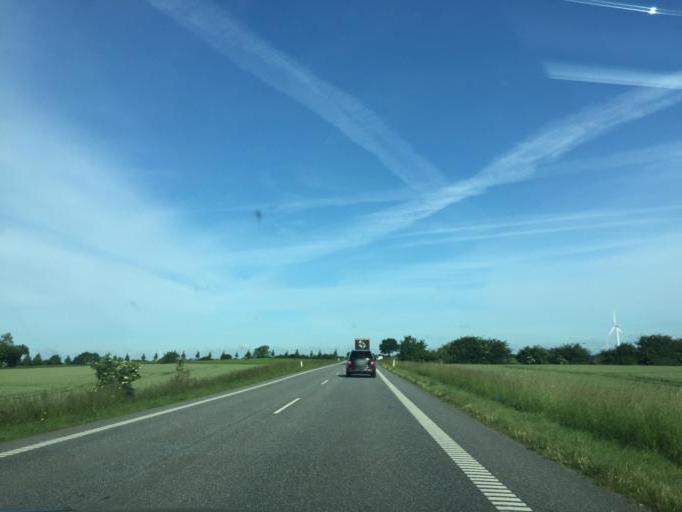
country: DK
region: South Denmark
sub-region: Middelfart Kommune
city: Ejby
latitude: 55.4577
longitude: 9.9450
